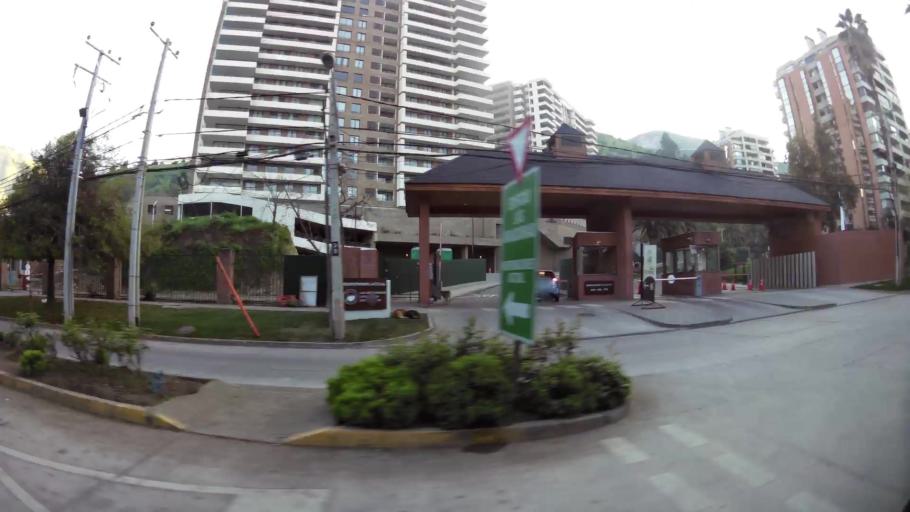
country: CL
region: Santiago Metropolitan
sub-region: Provincia de Santiago
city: Santiago
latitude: -33.3846
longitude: -70.6114
